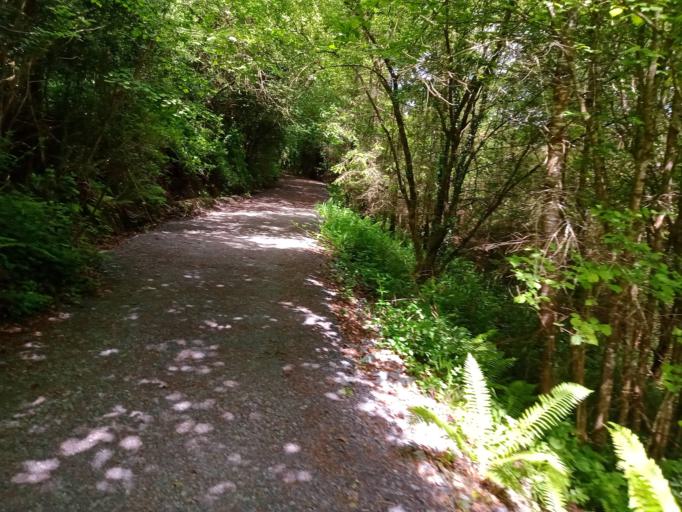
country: IE
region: Leinster
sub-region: Kilkenny
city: Thomastown
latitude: 52.4782
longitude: -7.0476
